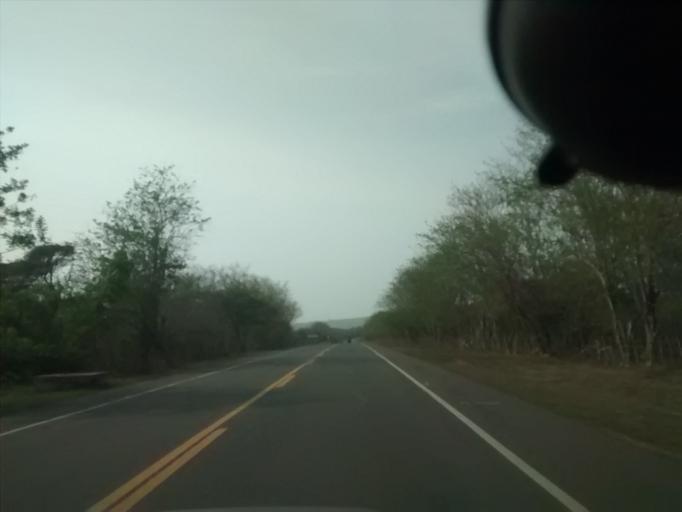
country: CO
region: Bolivar
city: Clemencia
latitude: 10.5828
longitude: -75.4493
